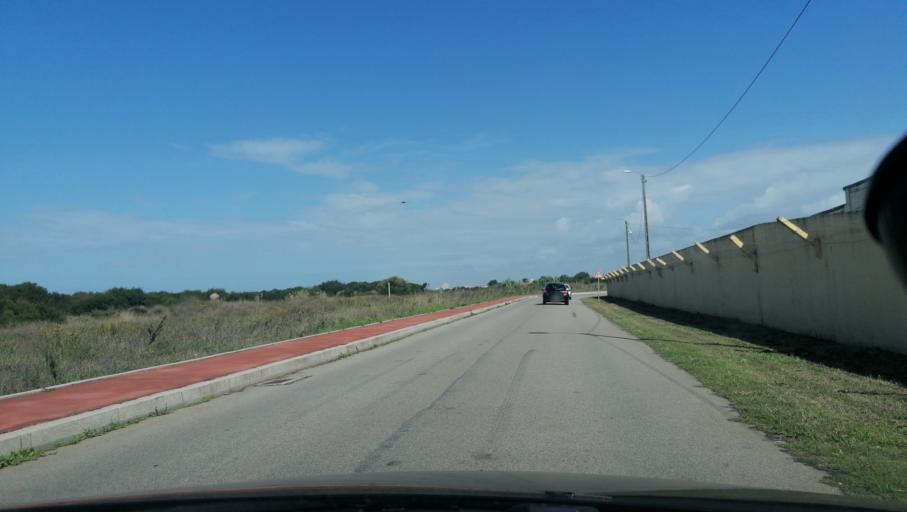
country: PT
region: Aveiro
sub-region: Espinho
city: Souto
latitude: 40.9791
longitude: -8.6432
